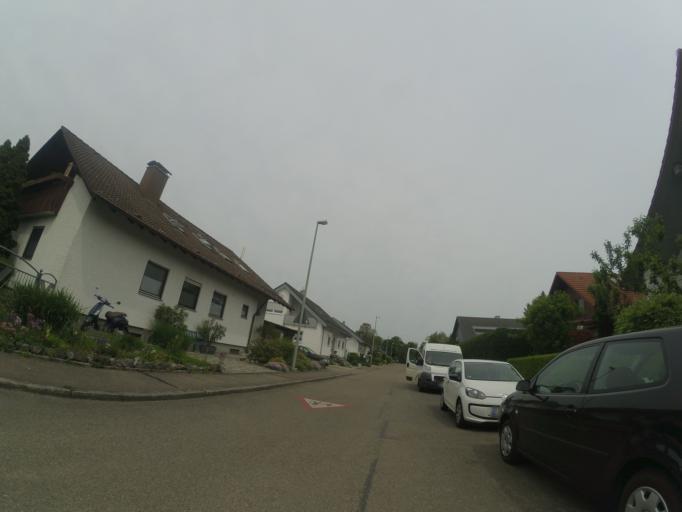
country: DE
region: Baden-Wuerttemberg
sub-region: Tuebingen Region
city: Staig
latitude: 48.3323
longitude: 9.9693
